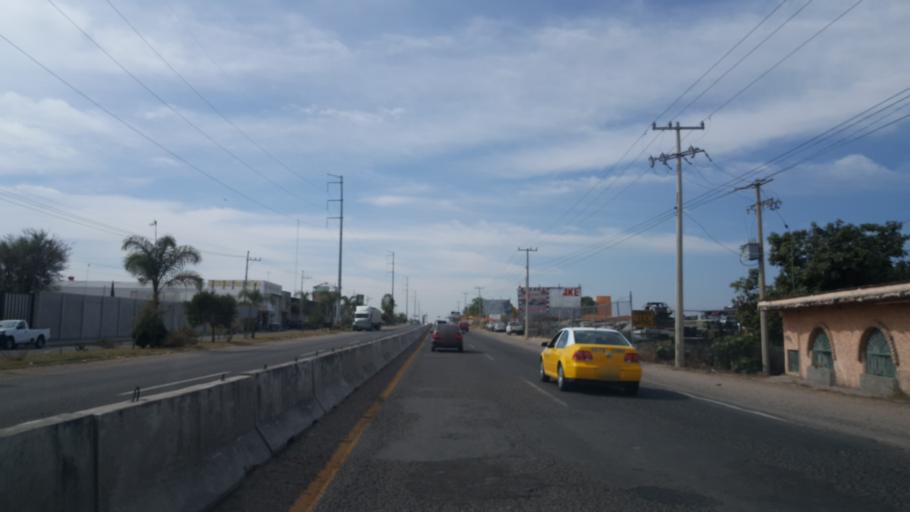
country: MX
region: Jalisco
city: San Juan de los Lagos
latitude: 21.2780
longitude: -102.2961
